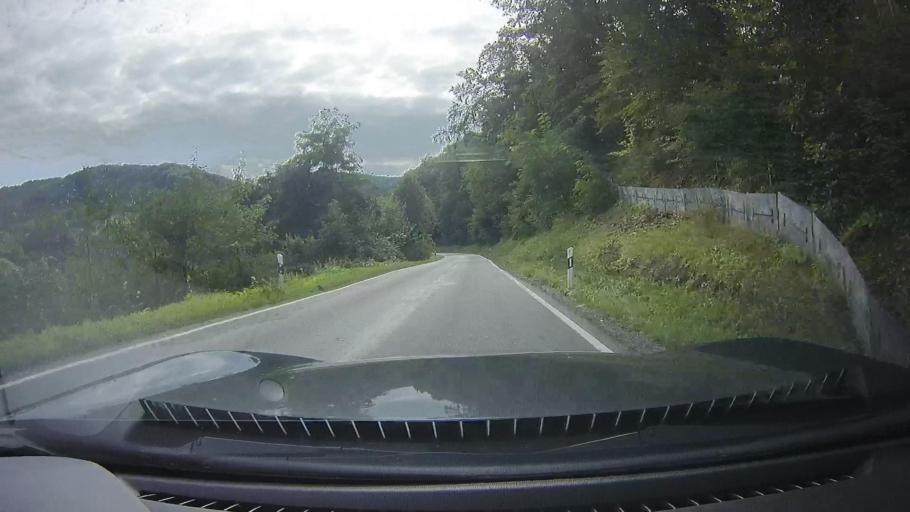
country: DE
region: Baden-Wuerttemberg
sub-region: Regierungsbezirk Stuttgart
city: Lowenstein
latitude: 49.0900
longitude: 9.3761
